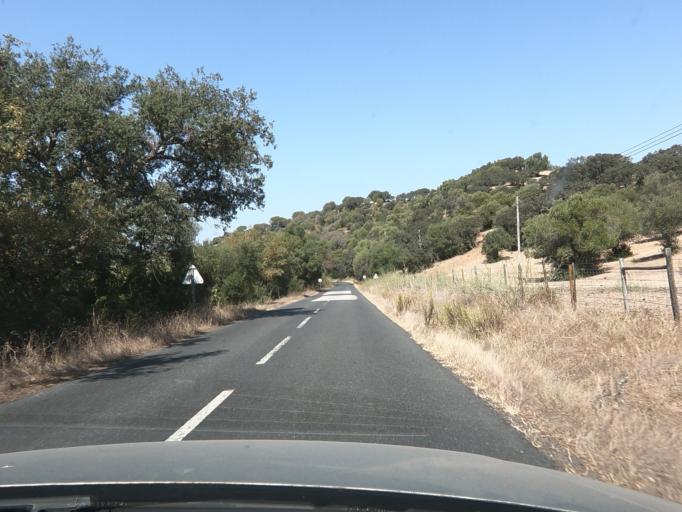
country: PT
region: Setubal
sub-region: Alcacer do Sal
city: Alcacer do Sal
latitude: 38.2754
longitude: -8.3759
